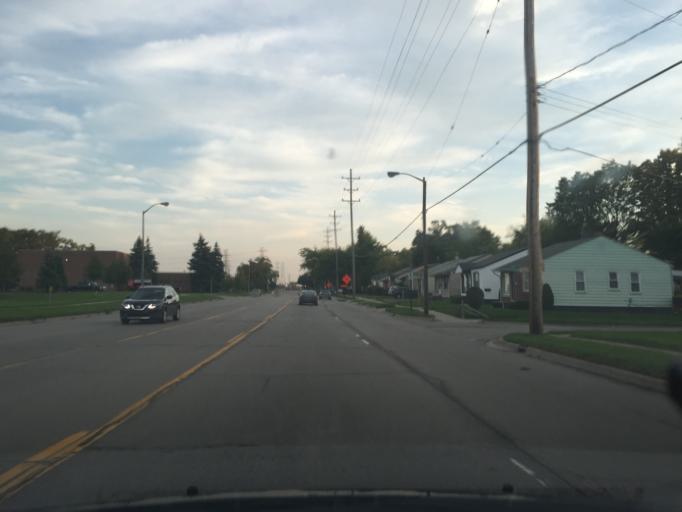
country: US
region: Michigan
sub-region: Oakland County
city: Pontiac
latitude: 42.6267
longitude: -83.2686
